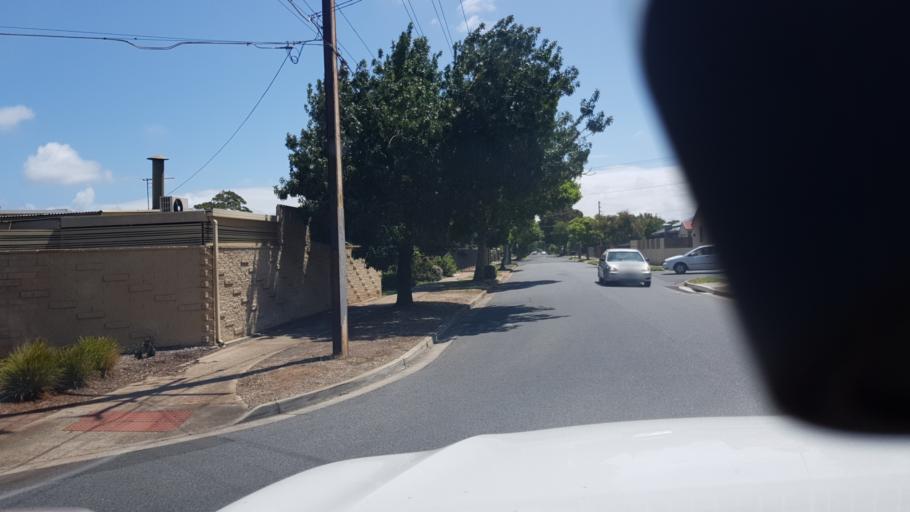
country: AU
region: South Australia
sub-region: Holdfast Bay
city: North Brighton
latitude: -35.0070
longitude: 138.5313
